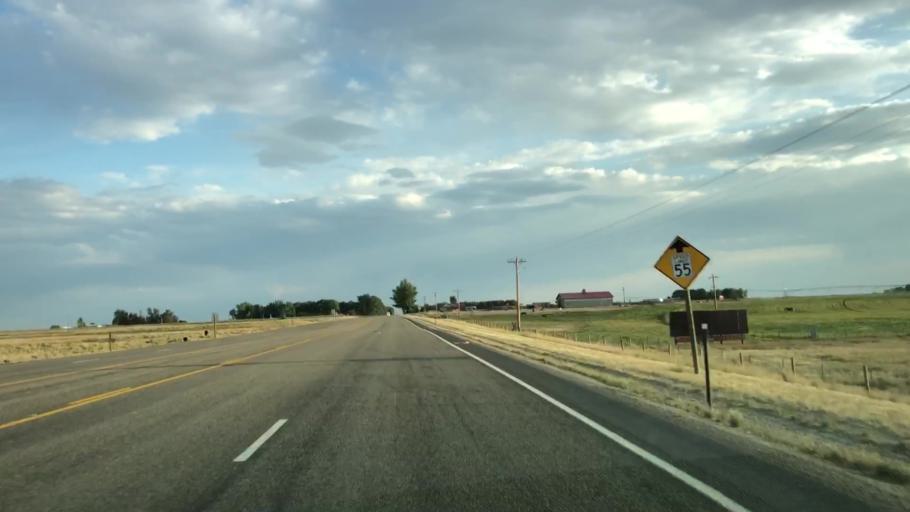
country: US
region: Wyoming
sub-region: Sweetwater County
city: North Rock Springs
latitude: 42.0631
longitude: -109.4382
